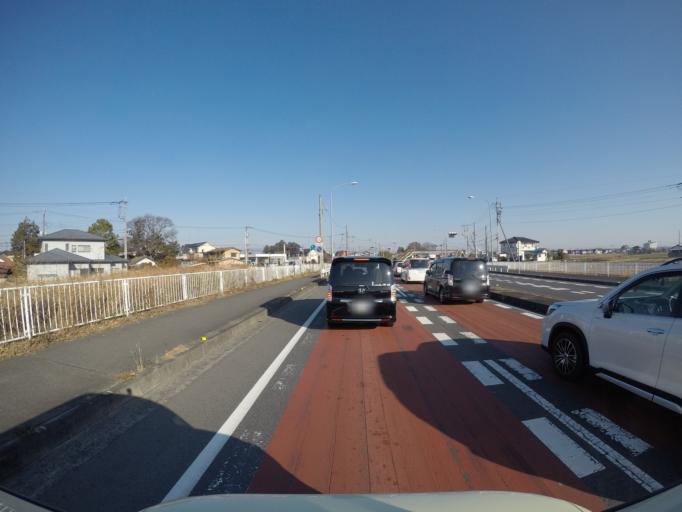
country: JP
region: Tochigi
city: Ujiie
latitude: 36.6712
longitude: 139.9599
